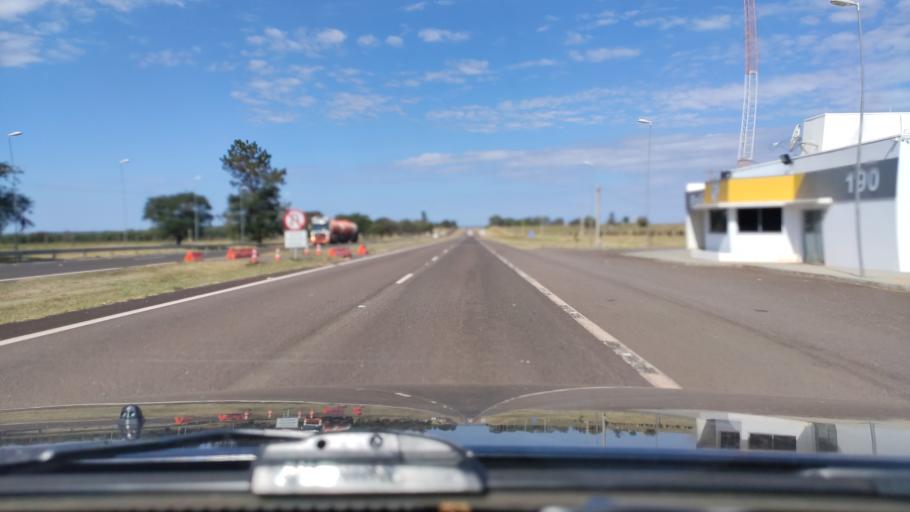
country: BR
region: Sao Paulo
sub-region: Rancharia
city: Rancharia
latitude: -22.4502
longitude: -50.9830
